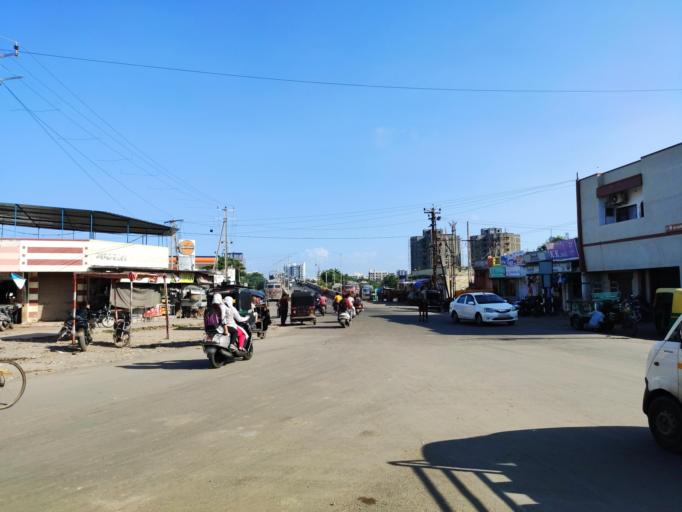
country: IN
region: Gujarat
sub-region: Jamnagar
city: Bedi
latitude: 22.4930
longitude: 70.0473
